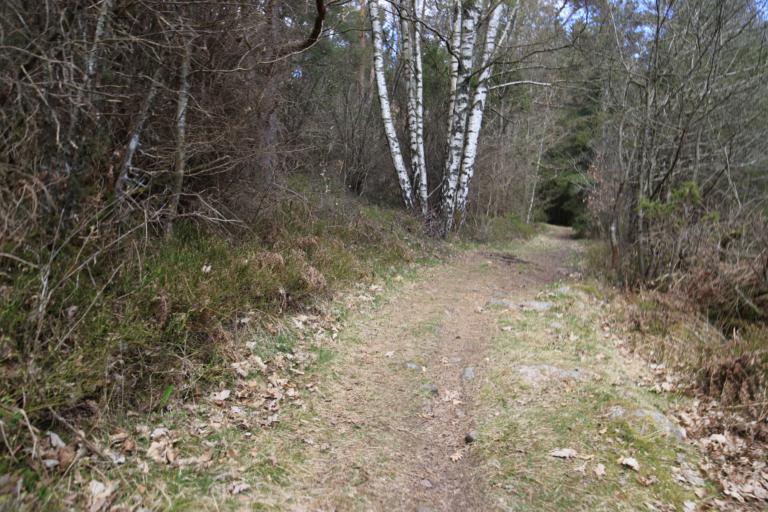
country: SE
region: Halland
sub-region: Varbergs Kommun
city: Varberg
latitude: 57.1784
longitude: 12.2351
